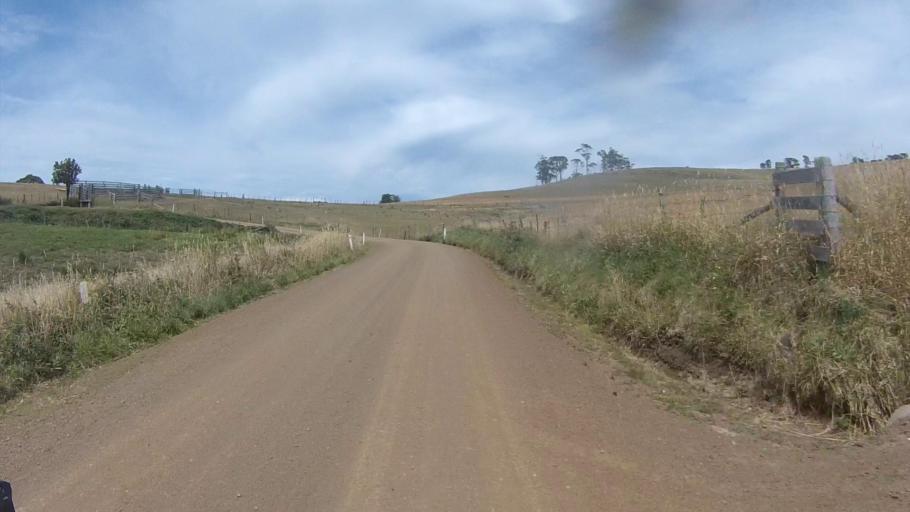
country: AU
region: Tasmania
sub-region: Sorell
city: Sorell
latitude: -42.7886
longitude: 147.8420
